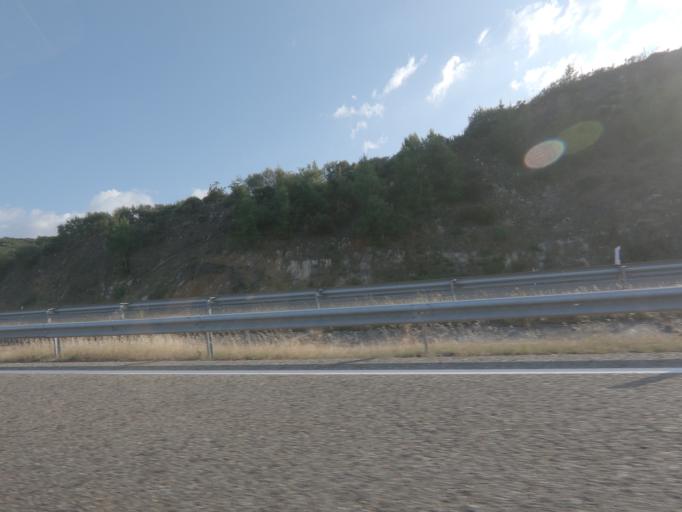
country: ES
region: Galicia
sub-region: Provincia de Ourense
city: Cualedro
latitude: 42.0078
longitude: -7.5677
